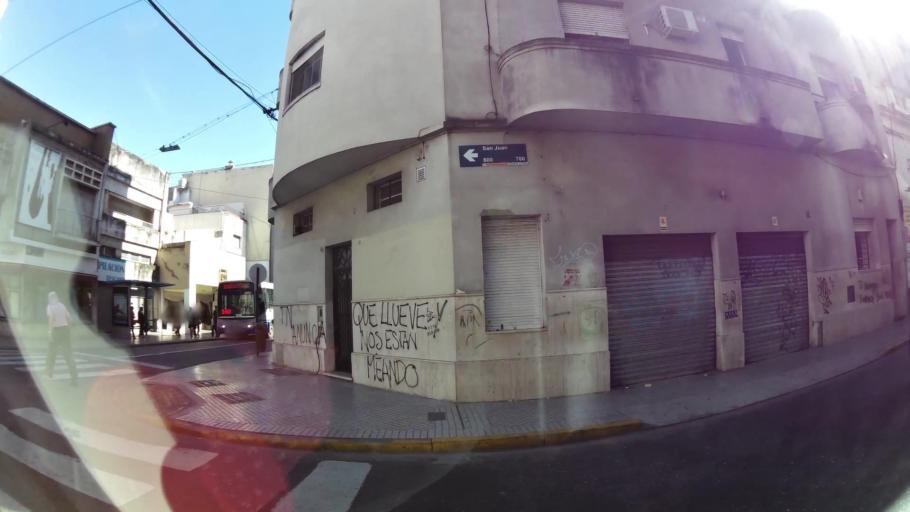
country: AR
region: Santa Fe
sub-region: Departamento de Rosario
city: Rosario
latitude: -32.9510
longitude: -60.6349
